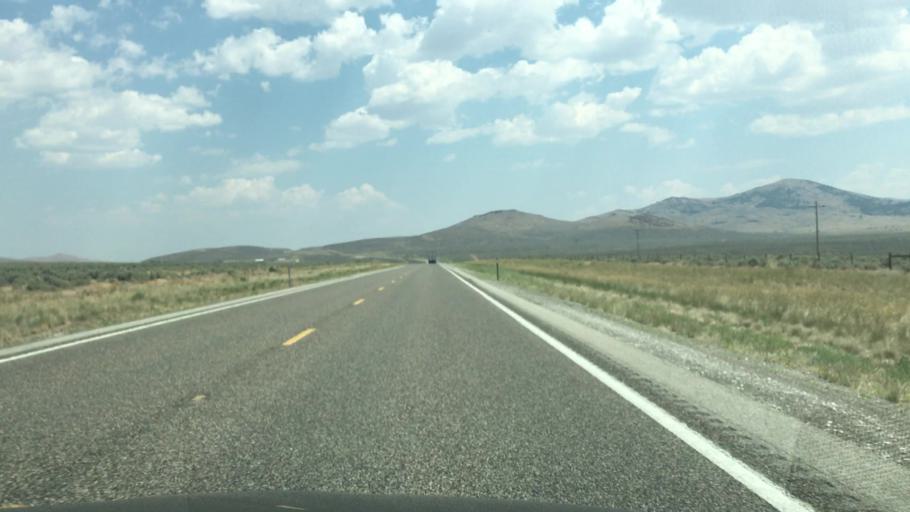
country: US
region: Nevada
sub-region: Elko County
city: Wells
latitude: 41.1636
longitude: -114.8902
